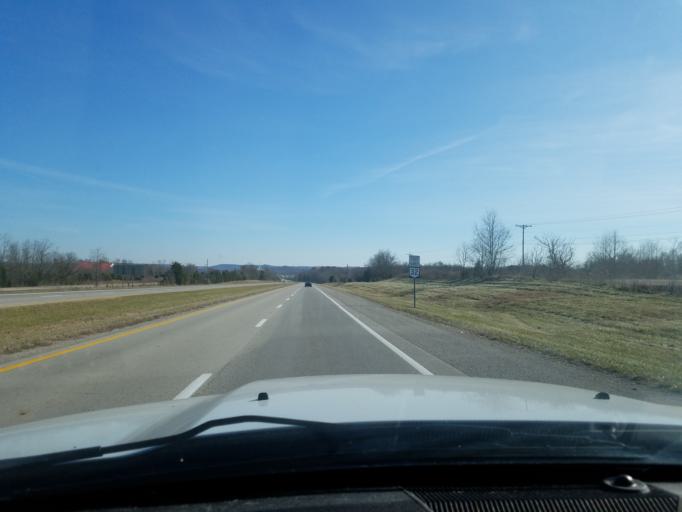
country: US
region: Ohio
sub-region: Adams County
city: Peebles
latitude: 38.9354
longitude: -83.4422
